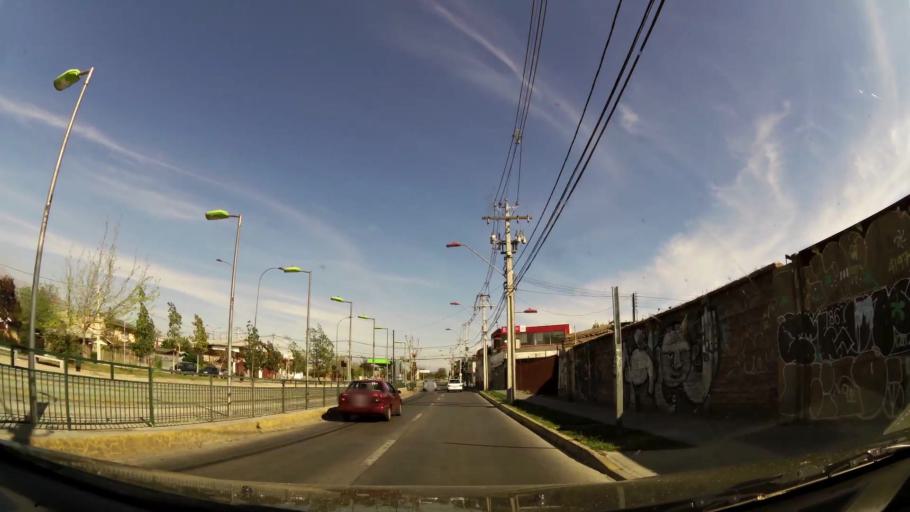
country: CL
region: Santiago Metropolitan
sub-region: Provincia de Santiago
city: Santiago
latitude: -33.4954
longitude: -70.6288
